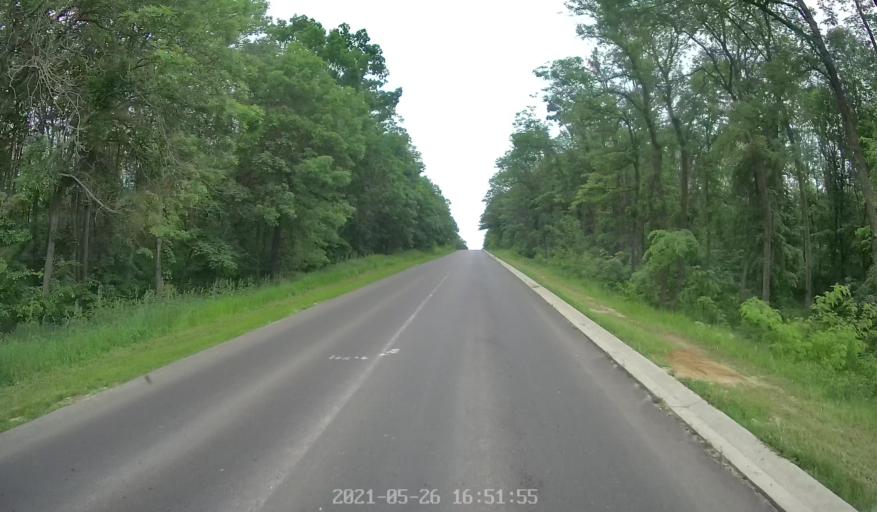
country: MD
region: Hincesti
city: Hincesti
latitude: 46.8629
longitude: 28.5077
